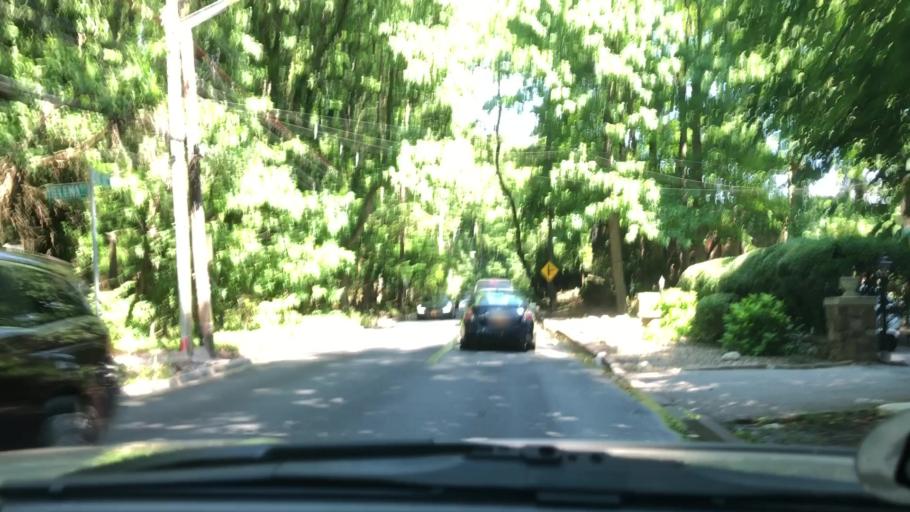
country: US
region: New York
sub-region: Richmond County
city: Staten Island
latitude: 40.5962
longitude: -74.1108
